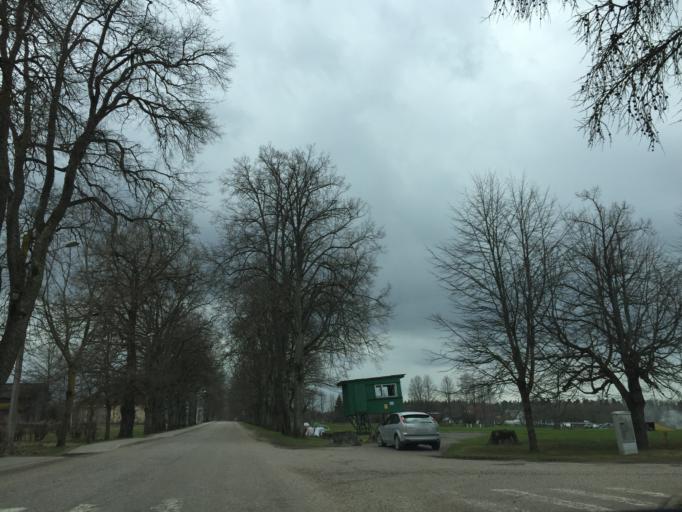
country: LV
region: Priekuli
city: Priekuli
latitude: 57.3524
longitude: 25.3320
